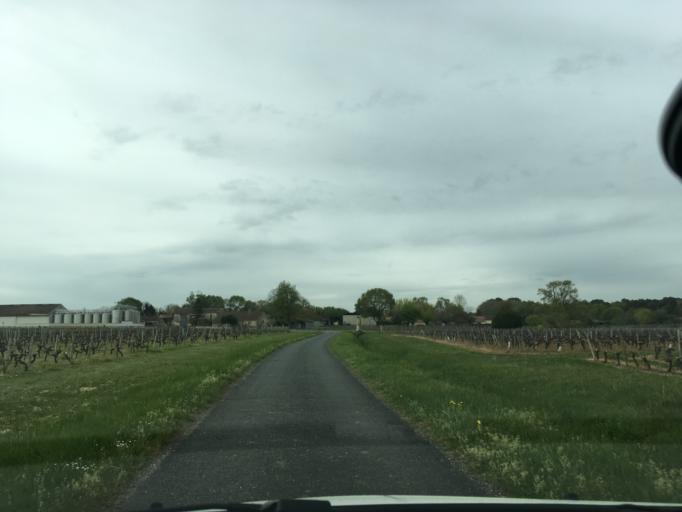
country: FR
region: Aquitaine
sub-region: Departement de la Gironde
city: Lesparre-Medoc
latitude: 45.3157
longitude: -0.8949
